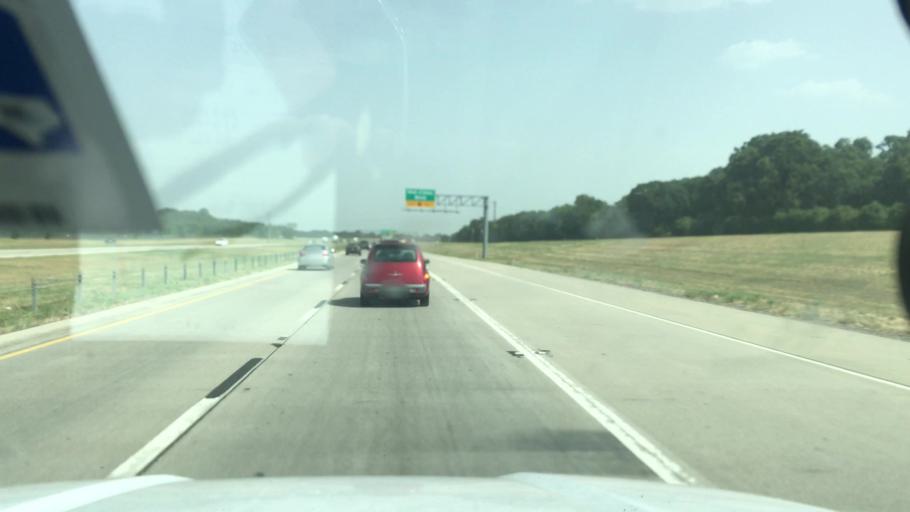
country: US
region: Texas
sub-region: Tarrant County
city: Euless
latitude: 32.8765
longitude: -97.0728
